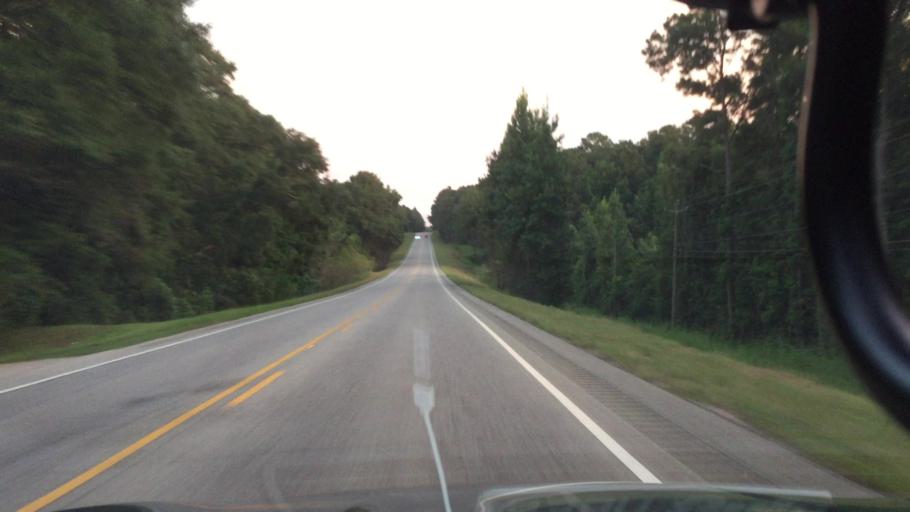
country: US
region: Alabama
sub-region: Coffee County
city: New Brockton
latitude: 31.3851
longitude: -85.8748
